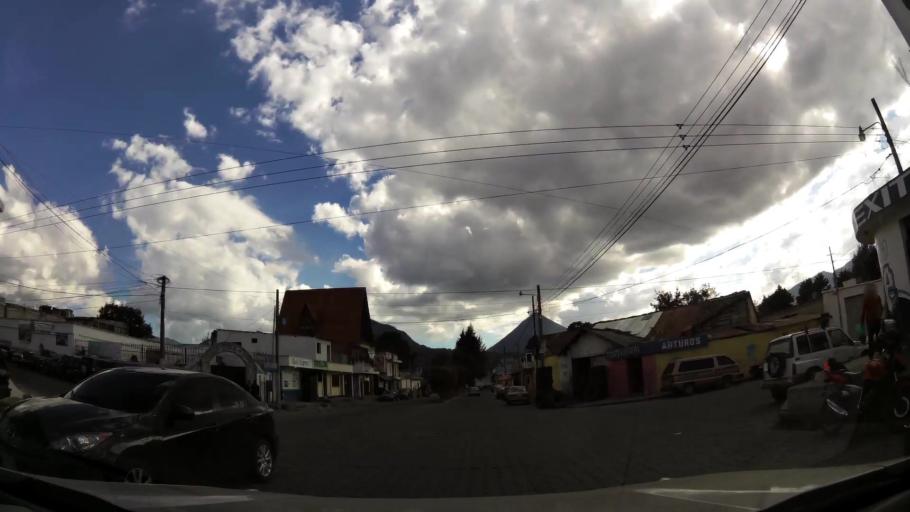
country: GT
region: Quetzaltenango
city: Quetzaltenango
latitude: 14.8470
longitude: -91.5268
